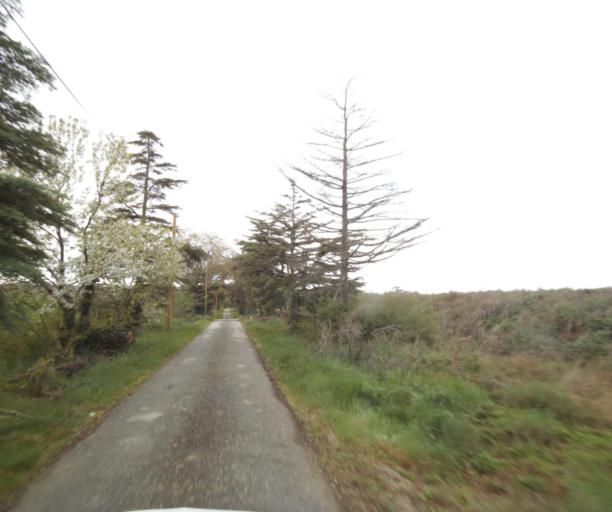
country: FR
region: Midi-Pyrenees
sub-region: Departement de l'Ariege
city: Saverdun
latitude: 43.2120
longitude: 1.6048
